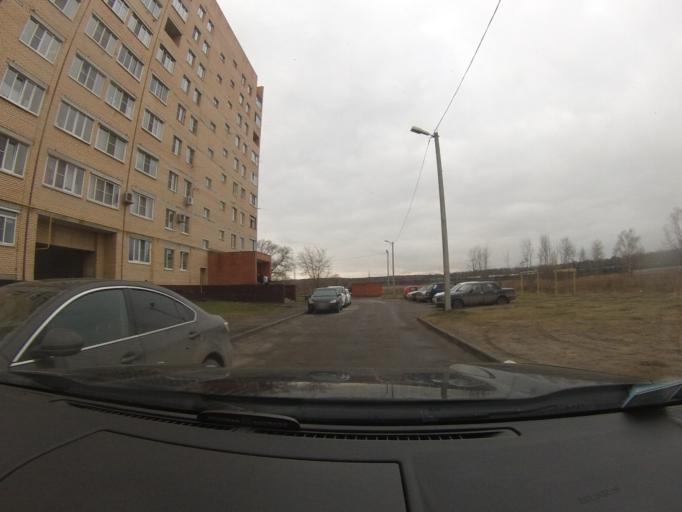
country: RU
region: Moskovskaya
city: Lopatinskiy
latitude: 55.3419
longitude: 38.7147
